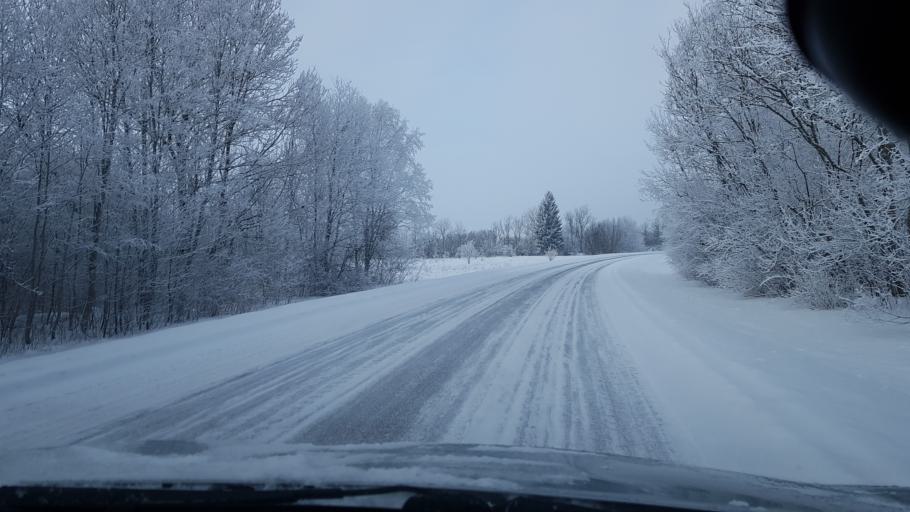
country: EE
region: Harju
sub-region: Keila linn
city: Keila
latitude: 59.3432
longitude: 24.4363
